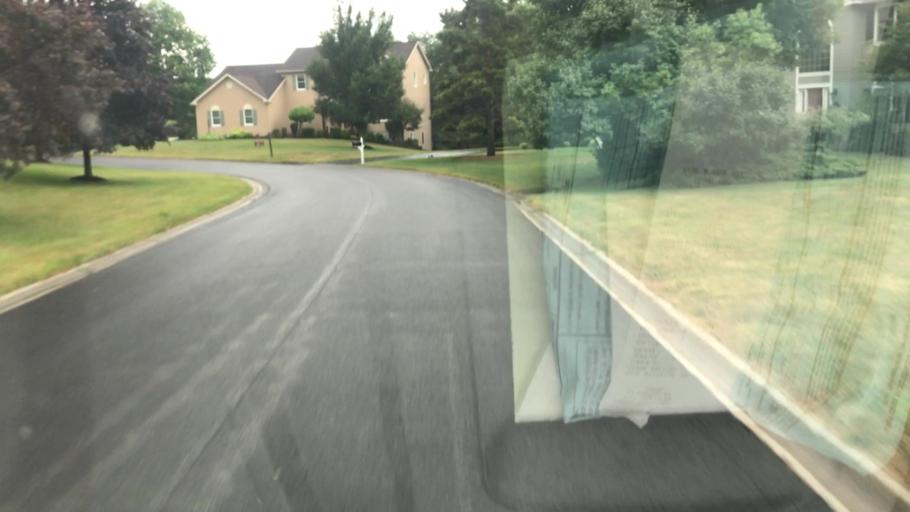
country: US
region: New York
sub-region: Onondaga County
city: Manlius
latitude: 42.9889
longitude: -75.9809
